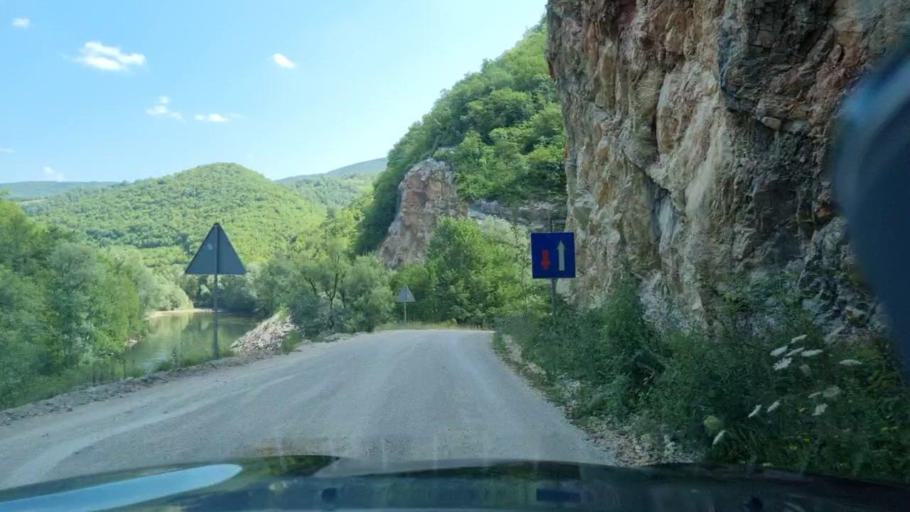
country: BA
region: Federation of Bosnia and Herzegovina
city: Kljuc
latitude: 44.5656
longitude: 16.8308
